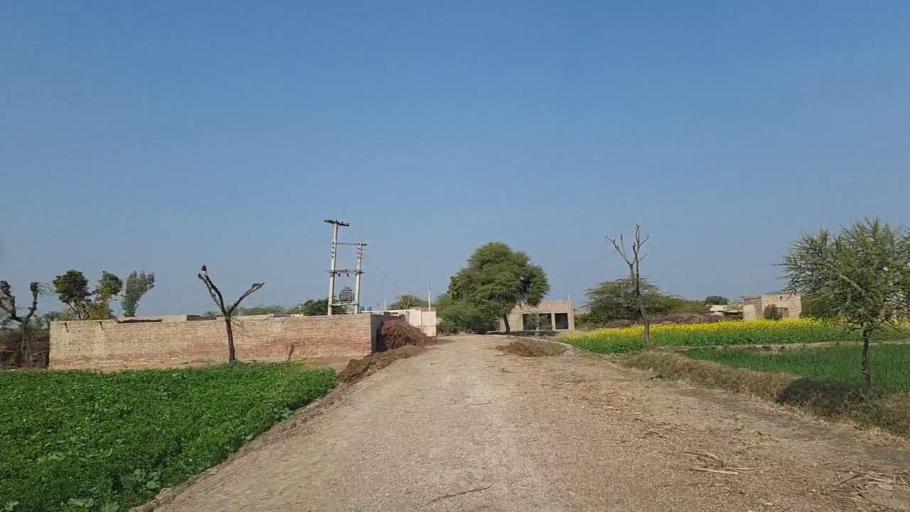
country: PK
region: Sindh
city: Jam Sahib
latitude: 26.2723
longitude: 68.5211
